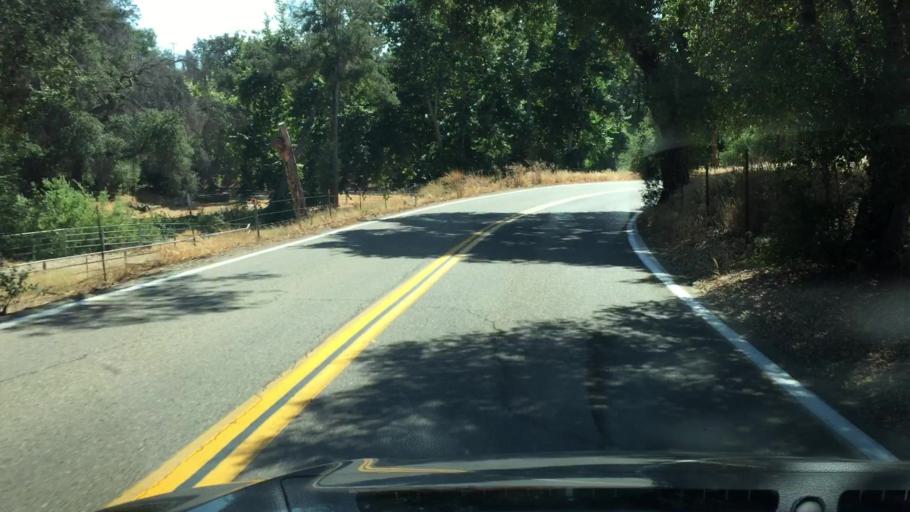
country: US
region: California
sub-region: San Diego County
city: Alpine
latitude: 32.7550
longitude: -116.7713
